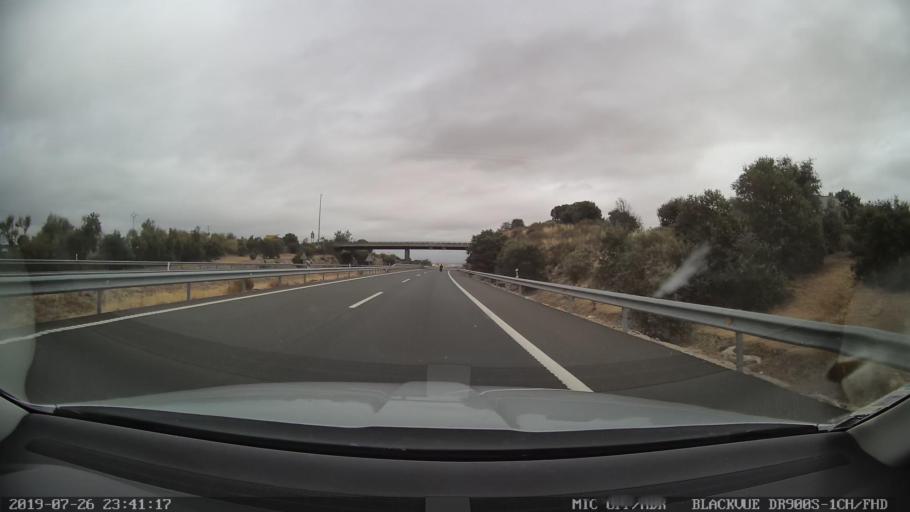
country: ES
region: Extremadura
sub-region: Provincia de Caceres
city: Trujillo
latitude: 39.4823
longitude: -5.8504
